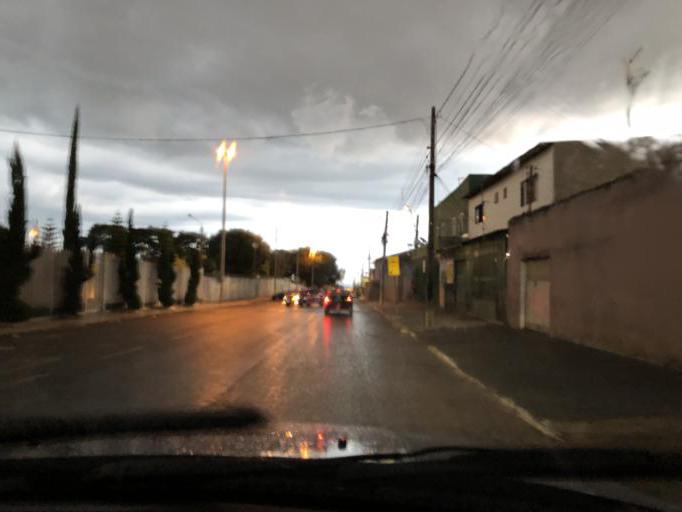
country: BR
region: Federal District
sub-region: Brasilia
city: Brasilia
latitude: -15.8072
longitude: -48.1167
